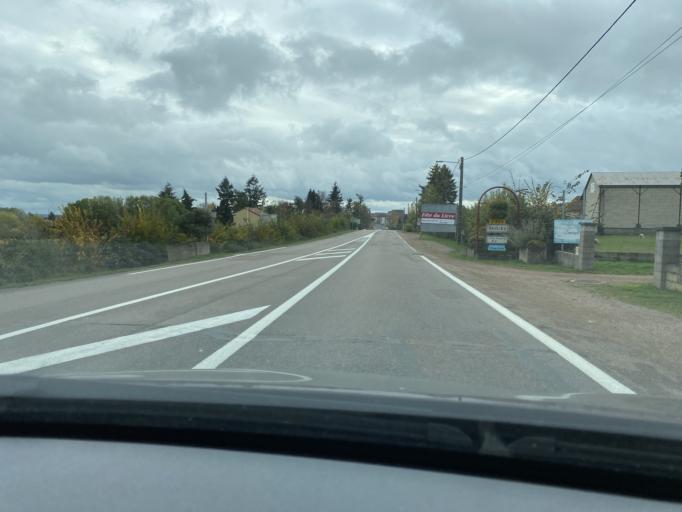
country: FR
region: Bourgogne
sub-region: Departement de la Cote-d'Or
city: Saulieu
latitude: 47.2879
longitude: 4.2235
